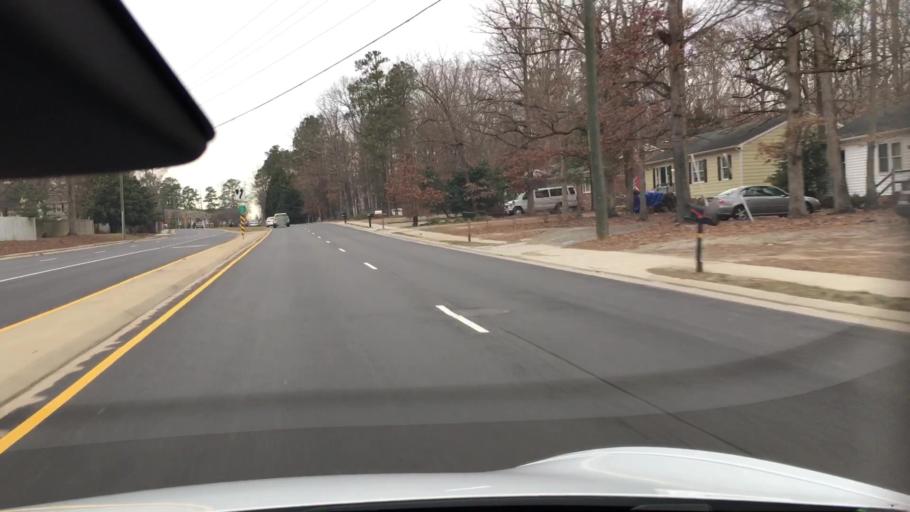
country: US
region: Virginia
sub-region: Chesterfield County
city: Bon Air
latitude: 37.5178
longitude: -77.5992
